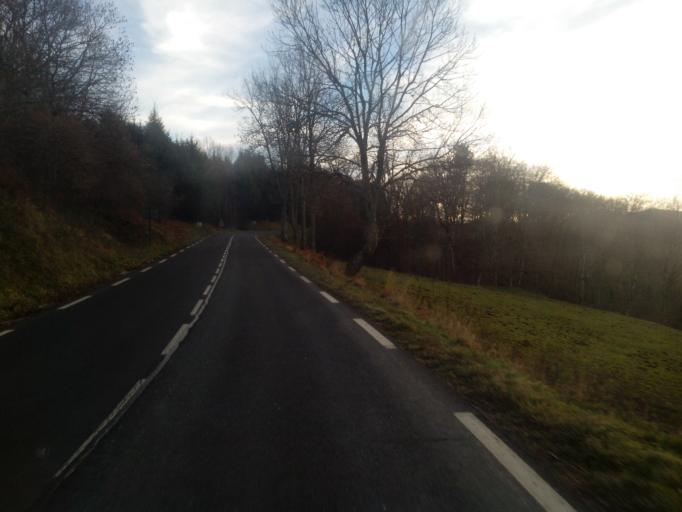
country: FR
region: Auvergne
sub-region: Departement du Cantal
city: Riom-es-Montagnes
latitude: 45.2739
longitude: 2.6663
